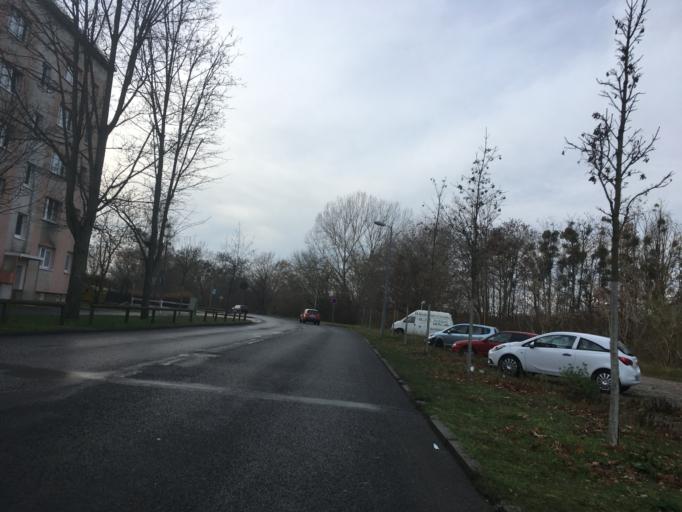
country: DE
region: Brandenburg
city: Eberswalde
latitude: 52.8408
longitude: 13.8117
